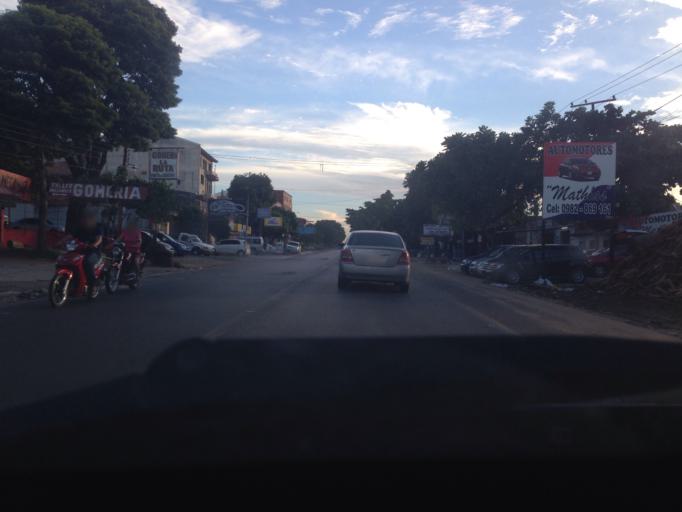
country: PY
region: Central
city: Lambare
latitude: -25.3456
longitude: -57.5885
